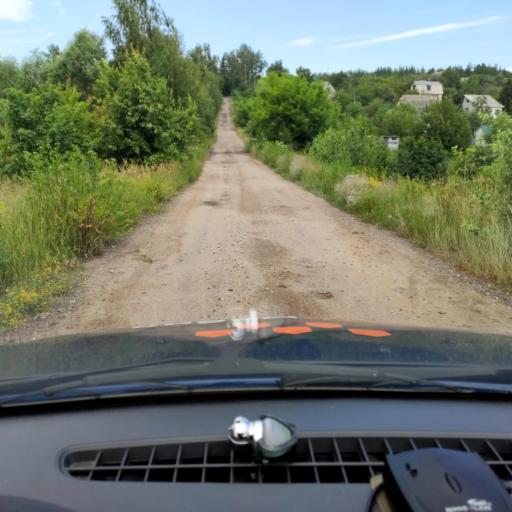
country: RU
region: Voronezj
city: Ramon'
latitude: 52.0749
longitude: 39.3187
